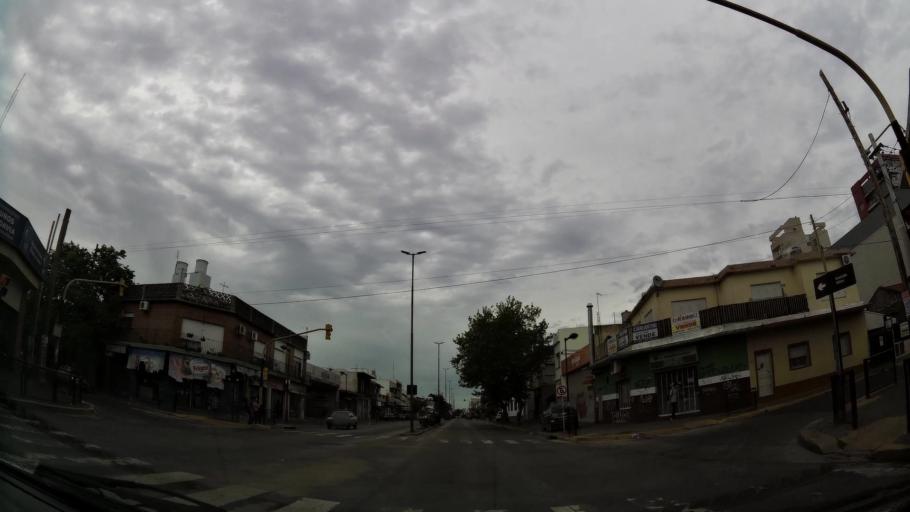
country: AR
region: Buenos Aires
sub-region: Partido de Quilmes
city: Quilmes
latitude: -34.7576
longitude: -58.2070
